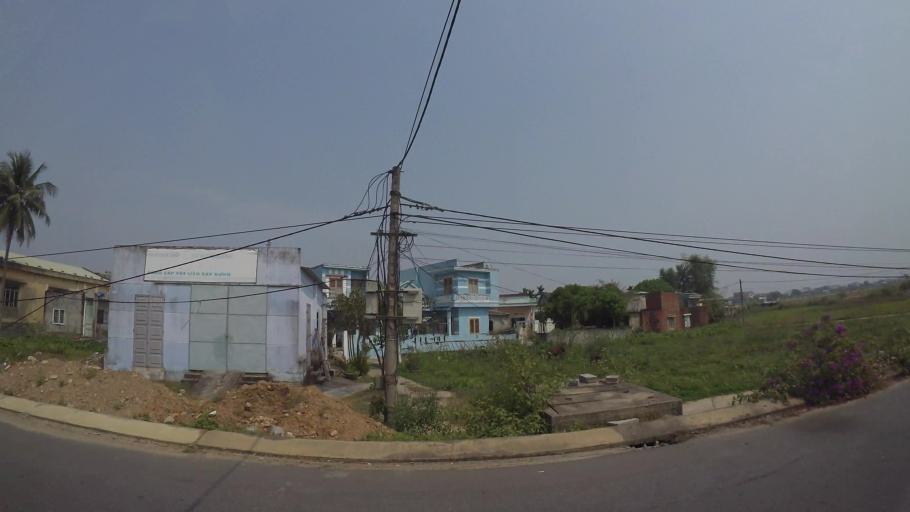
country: VN
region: Da Nang
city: Cam Le
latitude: 15.9750
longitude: 108.2094
